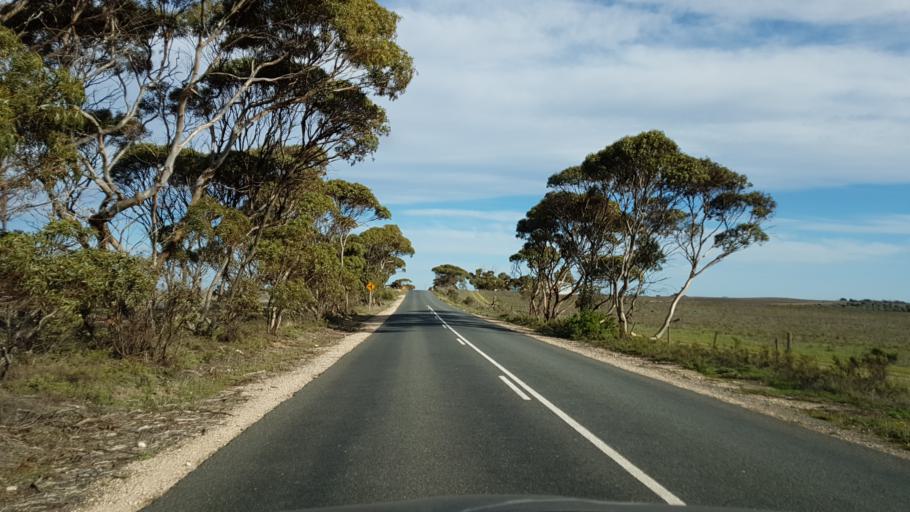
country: AU
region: South Australia
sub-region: Murray Bridge
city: Tailem Bend
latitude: -35.1832
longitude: 139.4581
